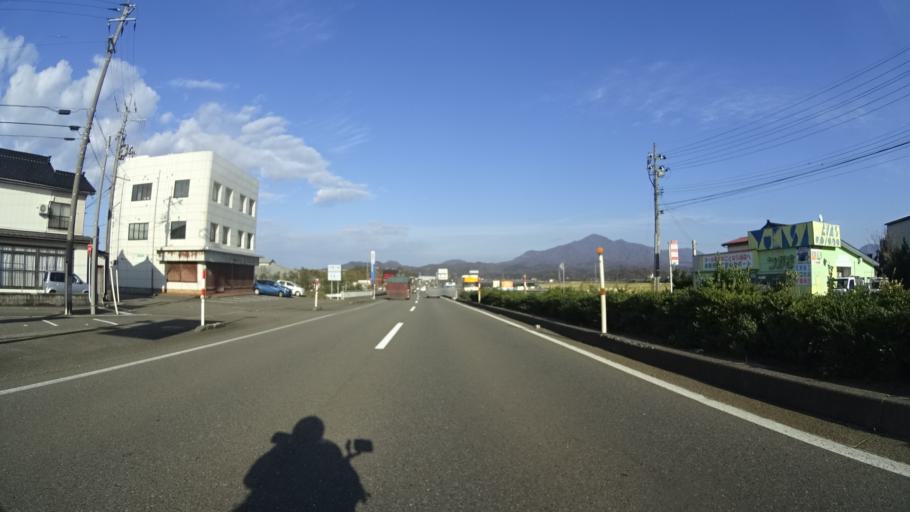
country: JP
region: Niigata
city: Joetsu
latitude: 37.2668
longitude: 138.3815
